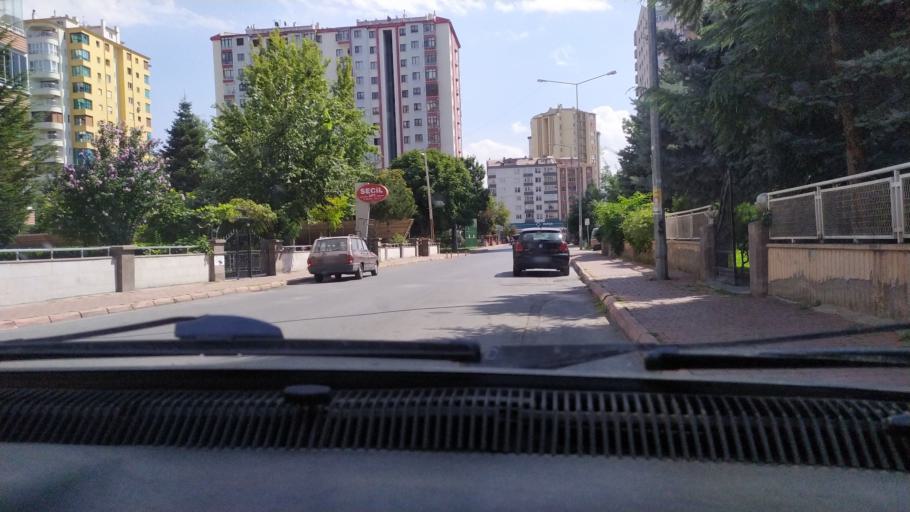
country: TR
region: Kayseri
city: Kayseri
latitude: 38.7283
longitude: 35.5222
